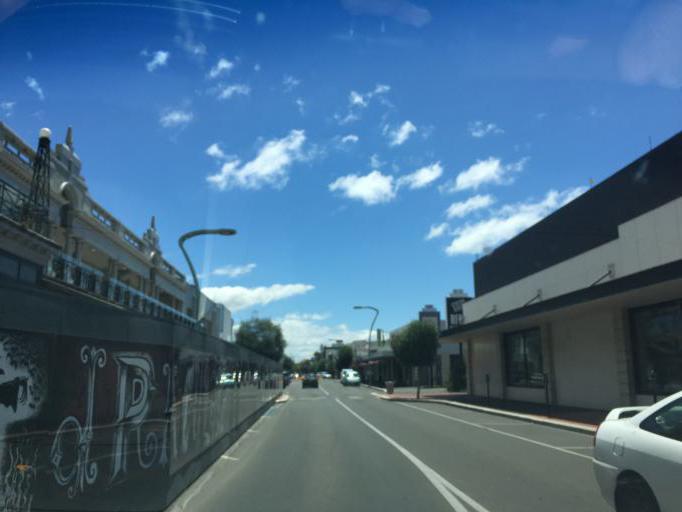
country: NZ
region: Hawke's Bay
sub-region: Hastings District
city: Hastings
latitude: -39.6445
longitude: 176.8460
